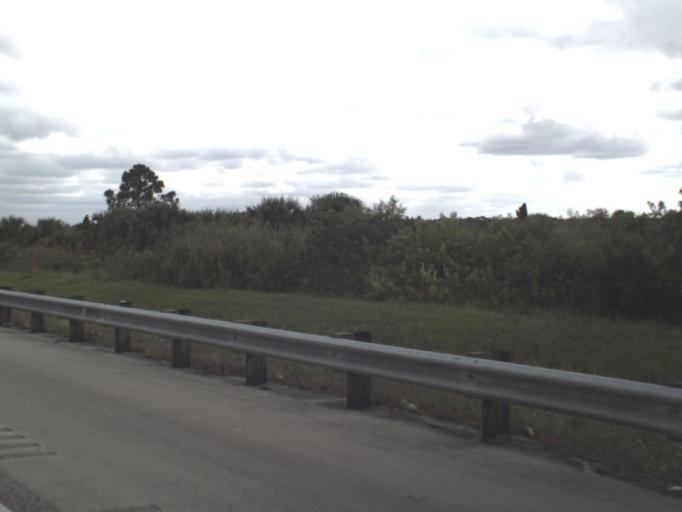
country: US
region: Florida
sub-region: Palm Beach County
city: Tequesta
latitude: 26.9830
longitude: -80.1865
